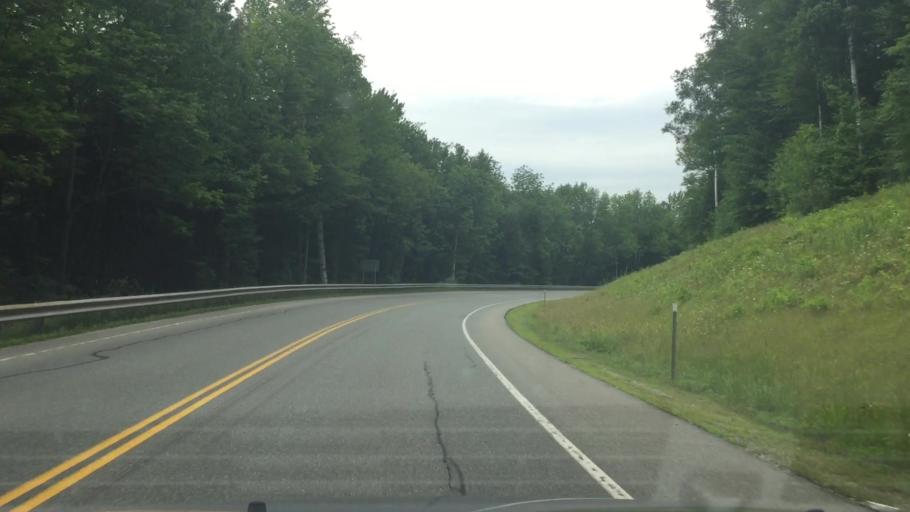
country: US
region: New Hampshire
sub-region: Grafton County
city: Deerfield
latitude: 44.2432
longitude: -71.6521
